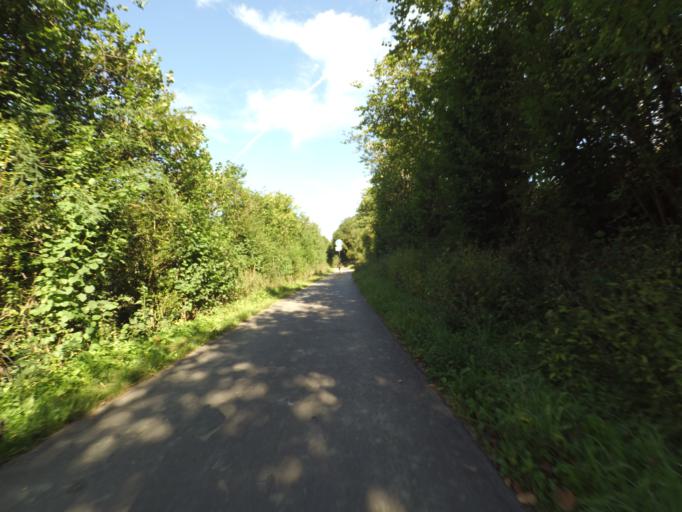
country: DE
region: Rheinland-Pfalz
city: Daun
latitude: 50.1885
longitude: 6.8167
